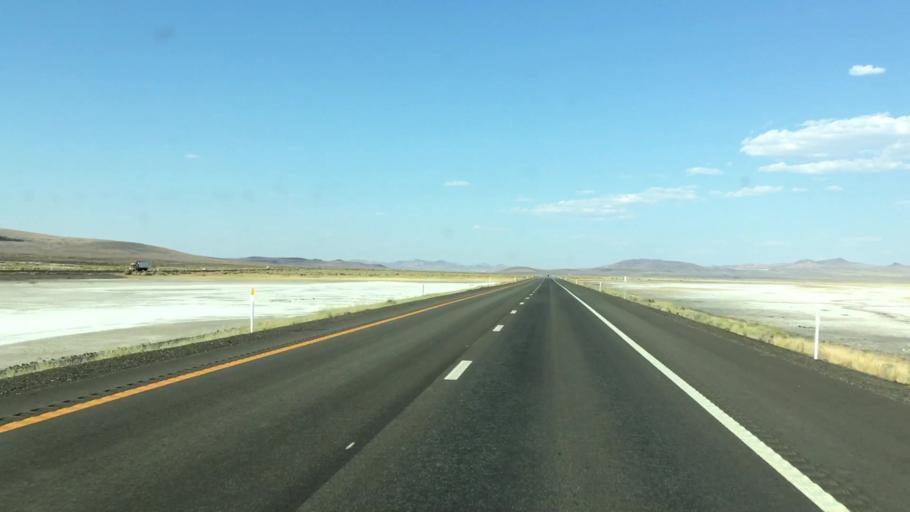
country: US
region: Nevada
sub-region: Lyon County
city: Fernley
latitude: 39.7052
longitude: -119.0944
